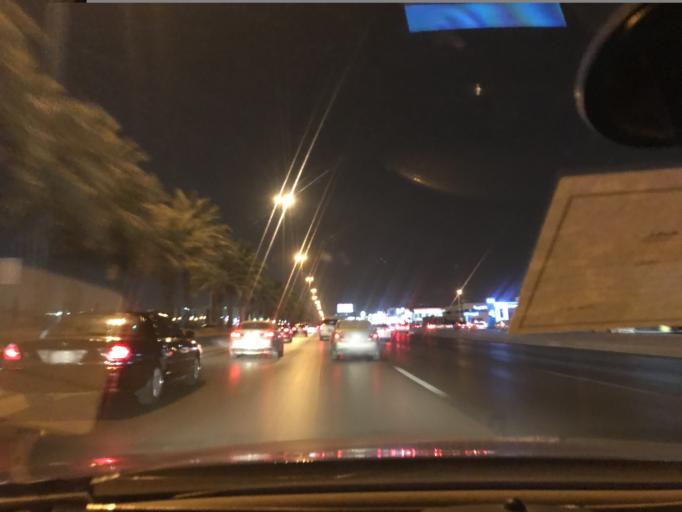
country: SA
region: Ar Riyad
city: Riyadh
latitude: 24.7509
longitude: 46.7434
